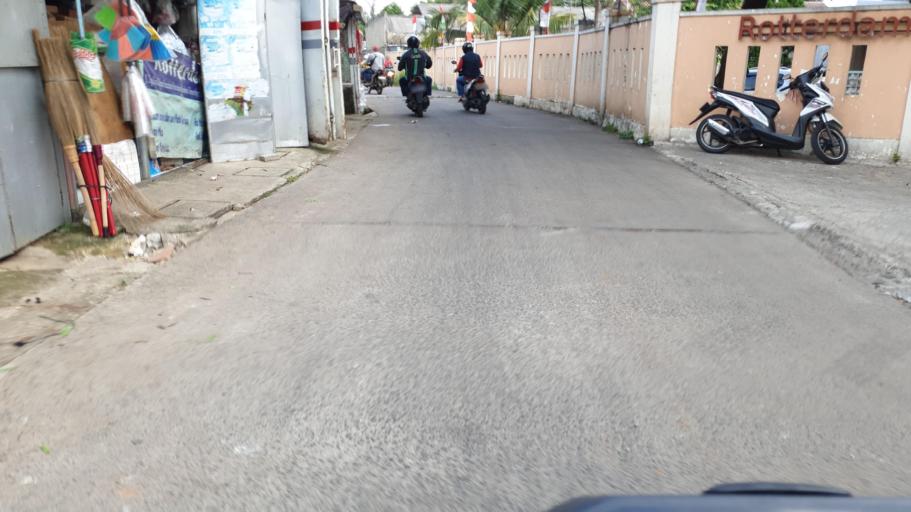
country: ID
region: West Java
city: Depok
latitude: -6.3675
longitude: 106.8498
